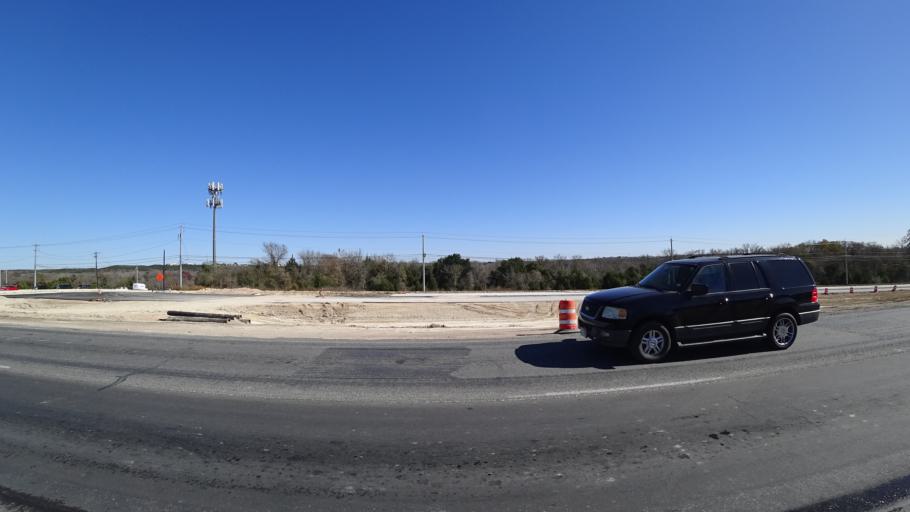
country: US
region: Texas
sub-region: Travis County
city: Austin
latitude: 30.3018
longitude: -97.6610
